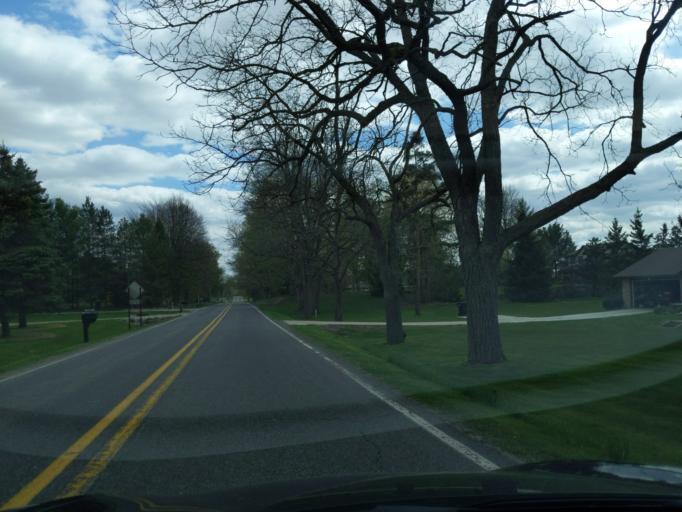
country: US
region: Michigan
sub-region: Ingham County
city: Holt
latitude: 42.6392
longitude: -84.4626
